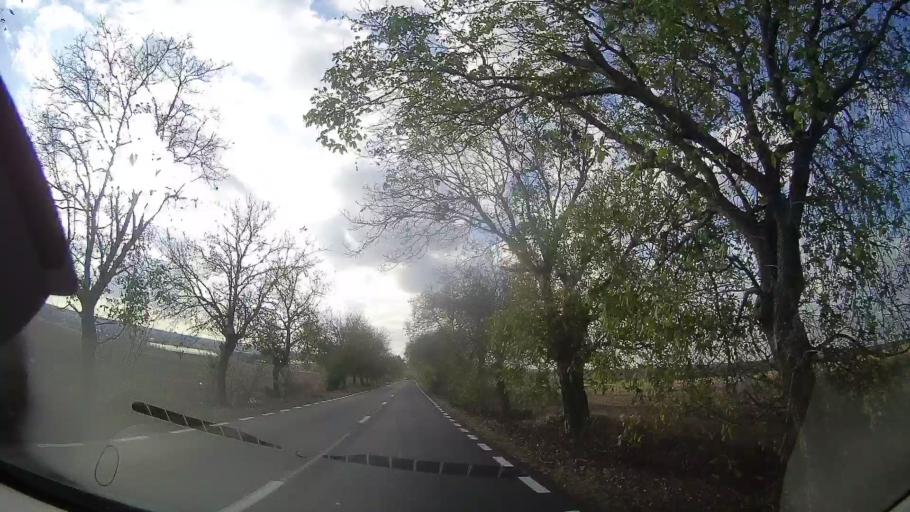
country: RO
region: Constanta
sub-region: Comuna Albesti
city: Albesti
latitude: 43.8132
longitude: 28.4432
